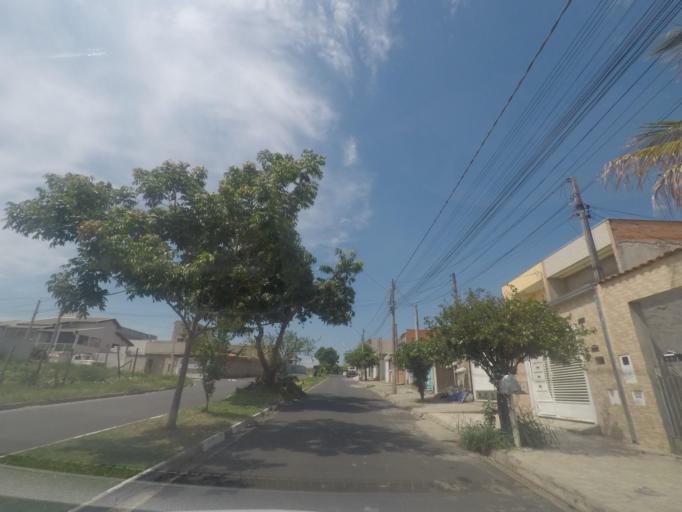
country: BR
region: Sao Paulo
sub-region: Sumare
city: Sumare
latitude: -22.7999
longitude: -47.2667
